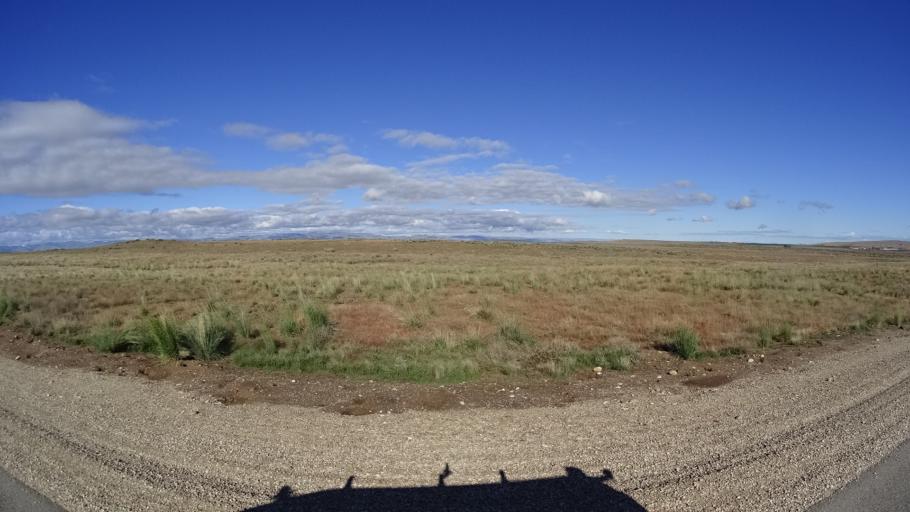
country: US
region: Idaho
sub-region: Ada County
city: Kuna
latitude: 43.3863
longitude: -116.4139
